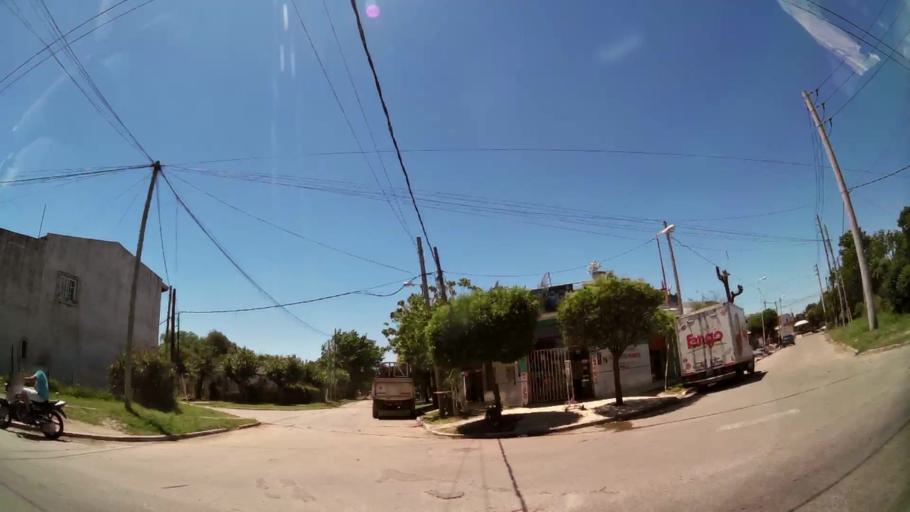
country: AR
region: Buenos Aires
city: Hurlingham
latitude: -34.5064
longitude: -58.7108
